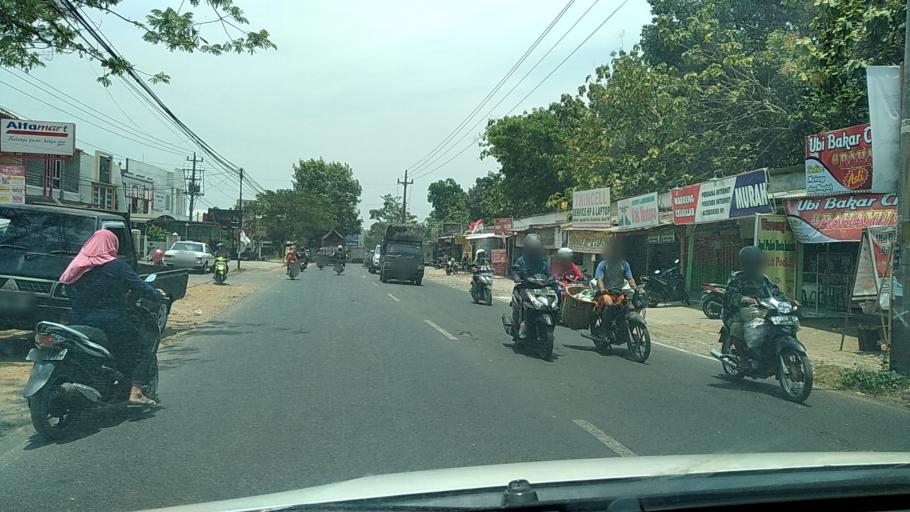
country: ID
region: Central Java
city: Ungaran
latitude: -7.0701
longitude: 110.3106
